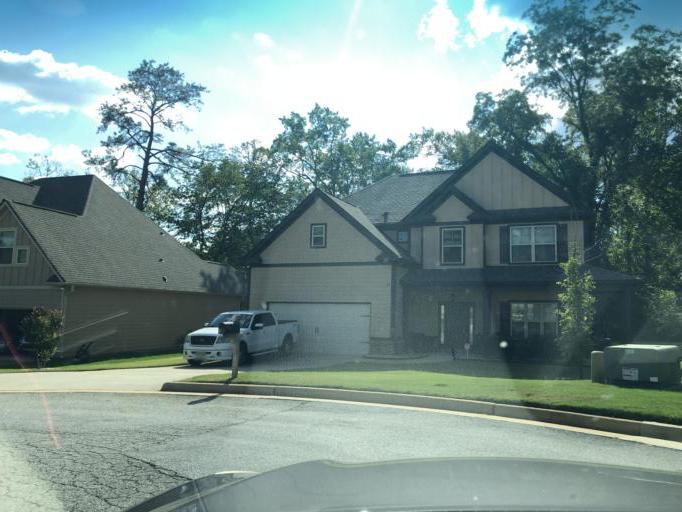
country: US
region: Georgia
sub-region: Muscogee County
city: Columbus
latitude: 32.5002
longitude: -84.9059
